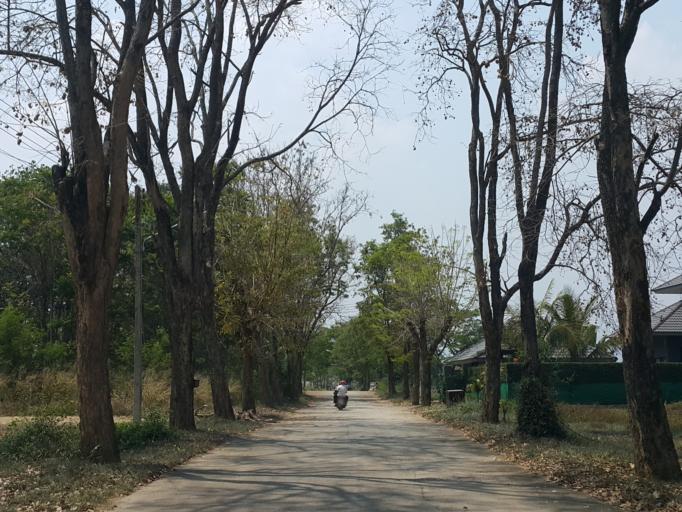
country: TH
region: Chiang Mai
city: Chiang Mai
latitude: 18.7330
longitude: 98.9705
